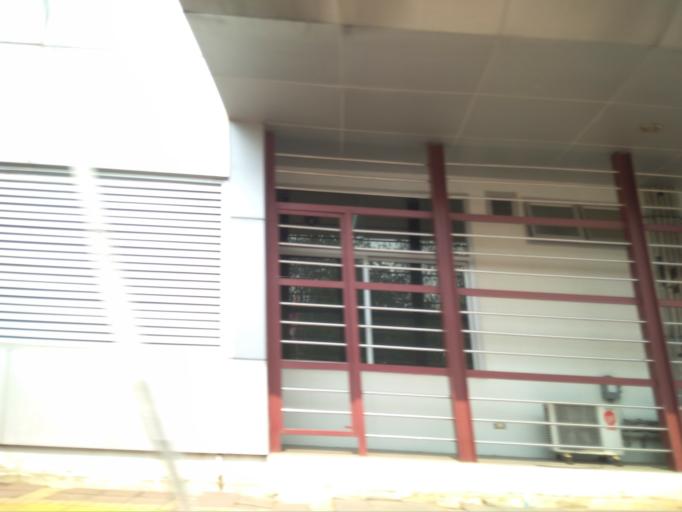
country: TH
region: Bangkok
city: Taling Chan
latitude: 13.7895
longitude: 100.4391
